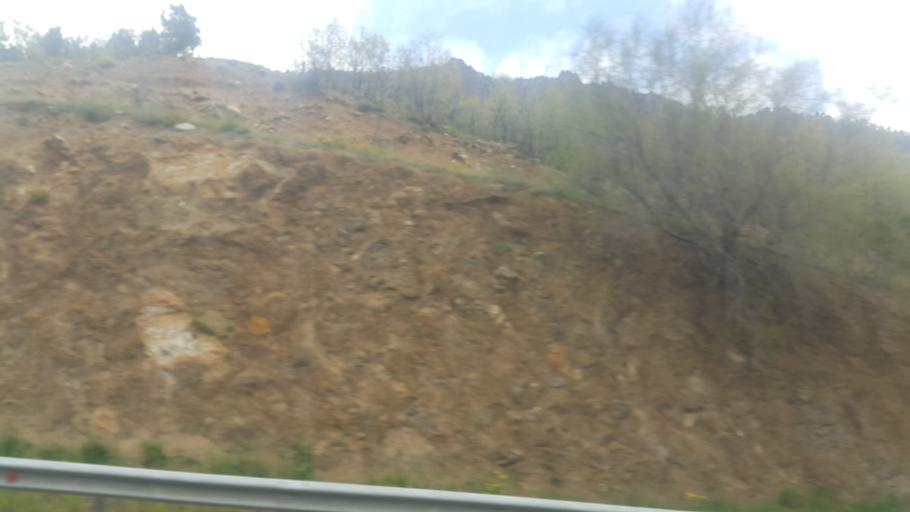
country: TR
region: Nigde
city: Ciftehan
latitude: 37.5335
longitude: 34.8047
